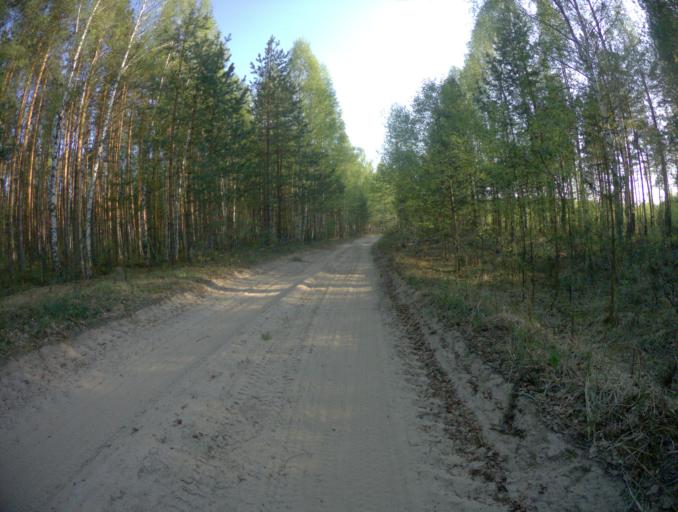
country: RU
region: Vladimir
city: Vyazniki
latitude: 56.3765
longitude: 42.1730
